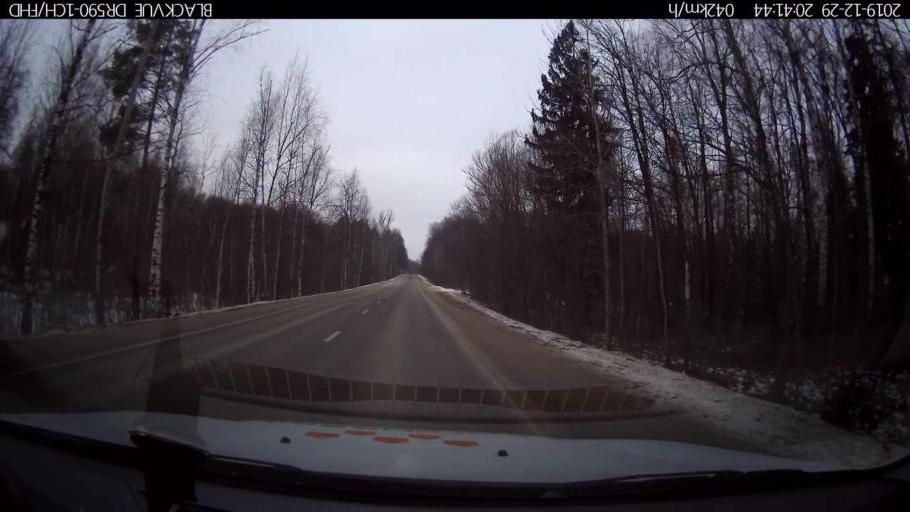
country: RU
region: Nizjnij Novgorod
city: Afonino
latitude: 56.1876
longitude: 44.0360
